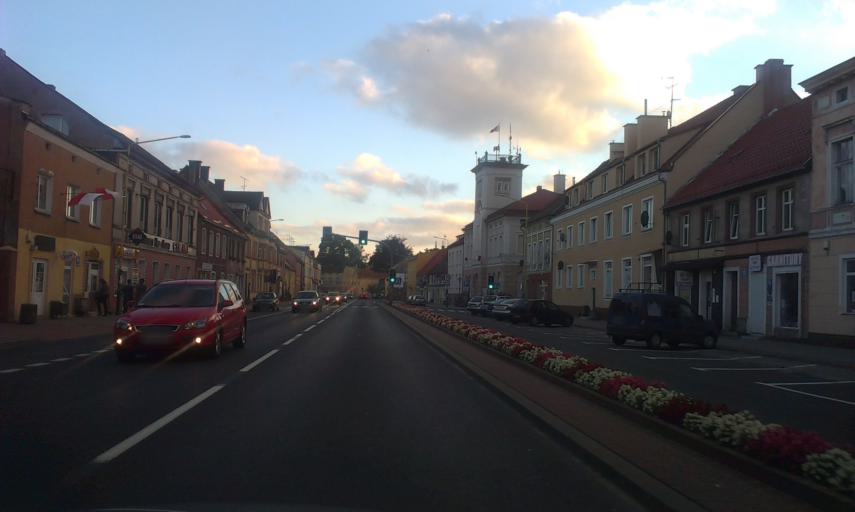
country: PL
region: West Pomeranian Voivodeship
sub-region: Powiat koszalinski
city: Sianow
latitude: 54.2279
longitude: 16.2936
